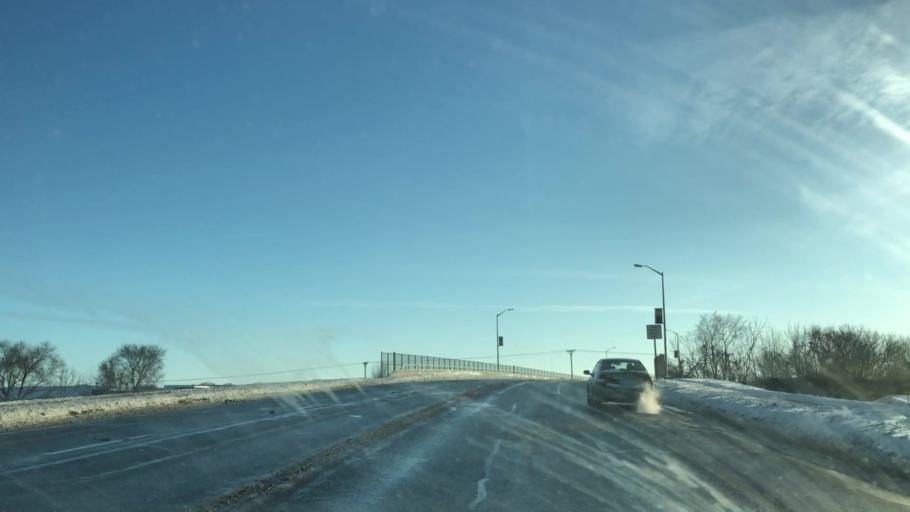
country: US
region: Iowa
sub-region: Marshall County
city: Marshalltown
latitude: 42.0421
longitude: -92.9180
